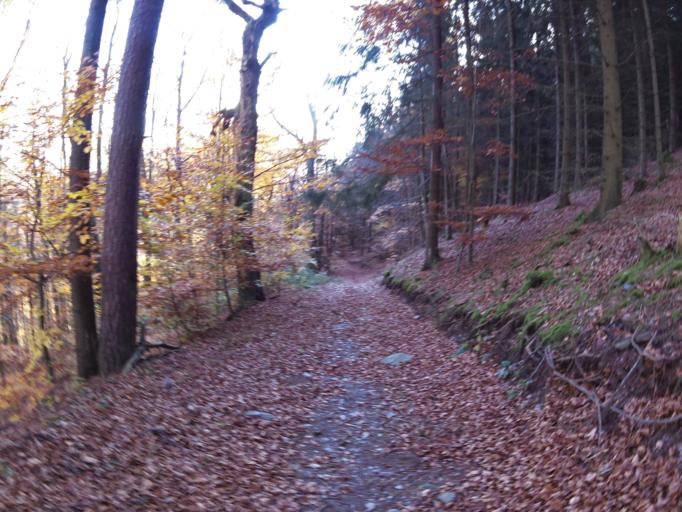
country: DE
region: Thuringia
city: Ruhla
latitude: 50.9066
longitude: 10.3668
